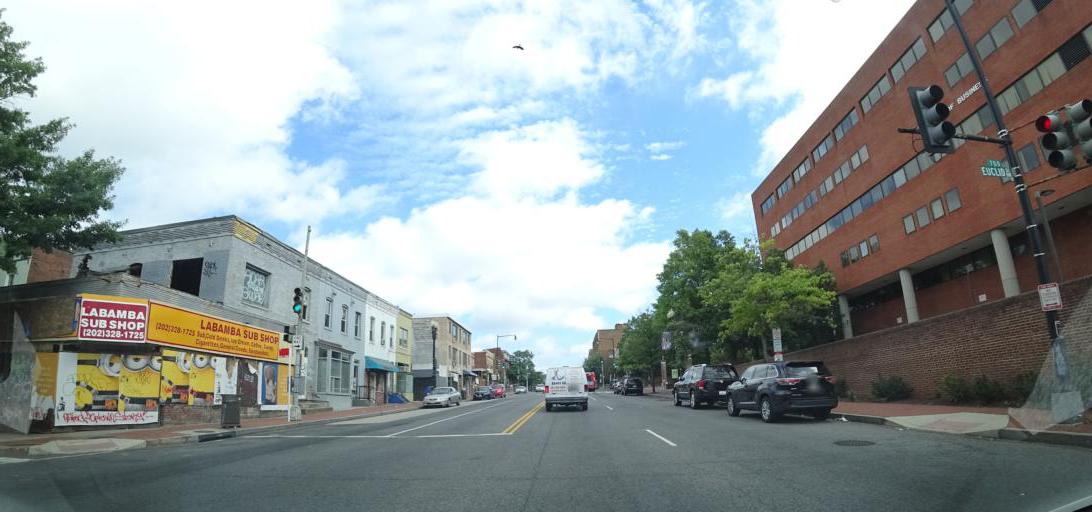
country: US
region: Washington, D.C.
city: Washington, D.C.
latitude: 38.9241
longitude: -77.0223
